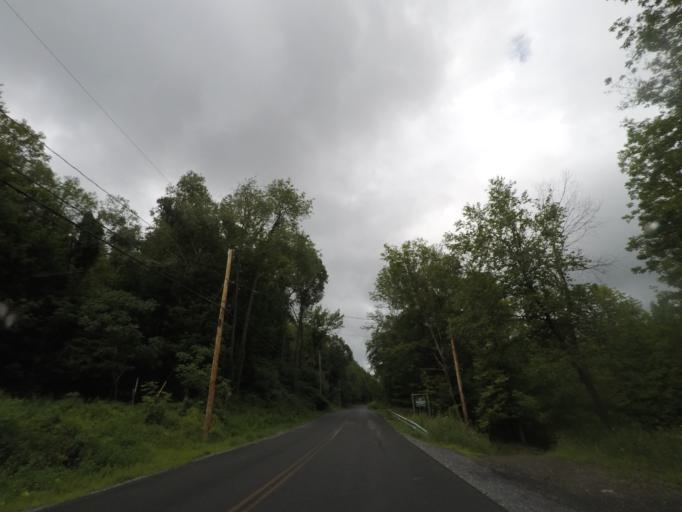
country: US
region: New York
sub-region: Rensselaer County
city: Averill Park
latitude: 42.6857
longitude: -73.3866
